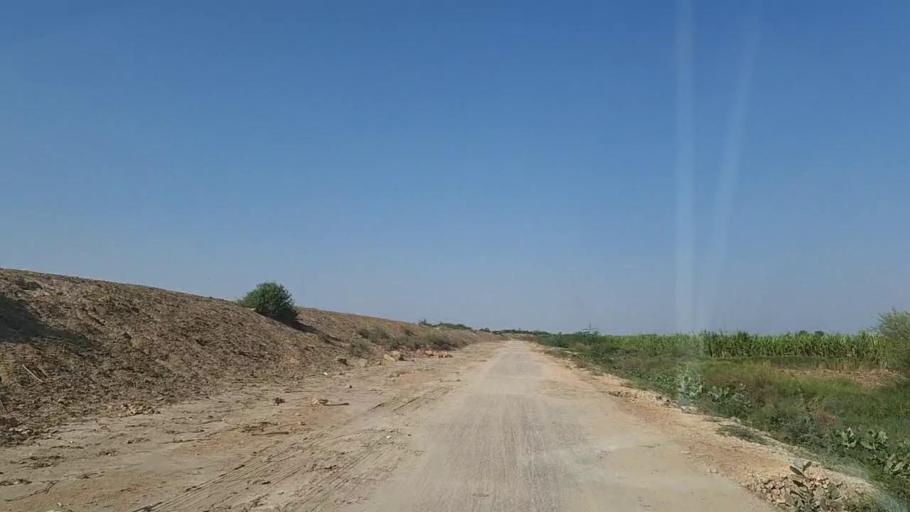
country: PK
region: Sindh
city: Chuhar Jamali
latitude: 24.5731
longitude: 68.0301
